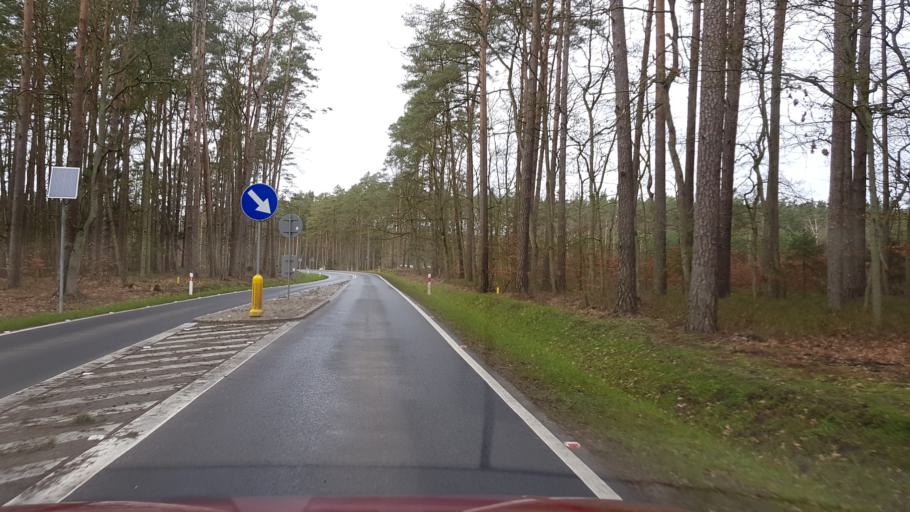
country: PL
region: West Pomeranian Voivodeship
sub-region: Powiat policki
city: Police
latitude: 53.6542
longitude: 14.4797
